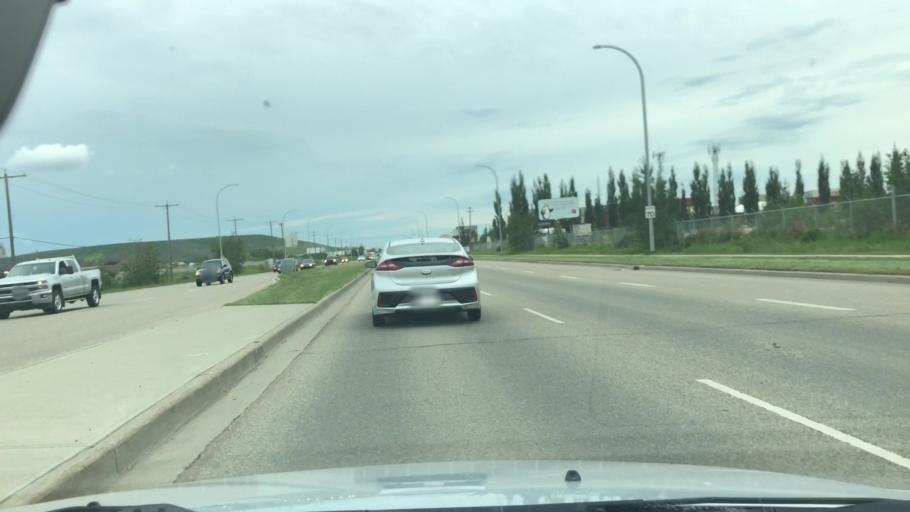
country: CA
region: Alberta
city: St. Albert
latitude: 53.5984
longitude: -113.6151
